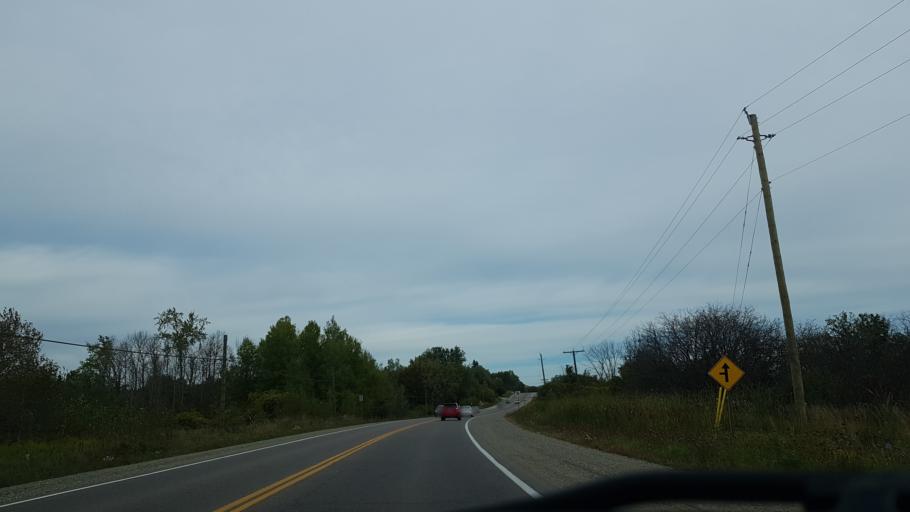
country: CA
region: Ontario
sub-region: Wellington County
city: Guelph
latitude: 43.5865
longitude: -80.2446
